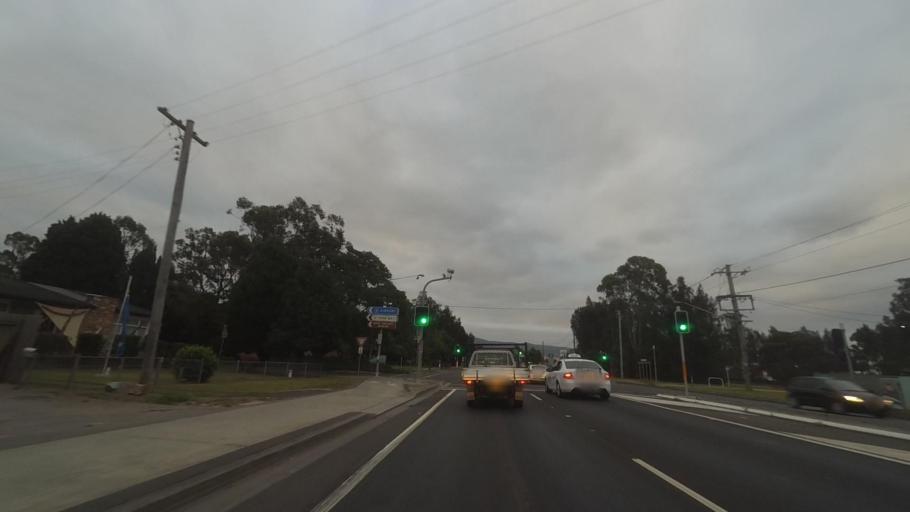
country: AU
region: New South Wales
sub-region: Shellharbour
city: Albion Park Rail
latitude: -34.5569
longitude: 150.7921
